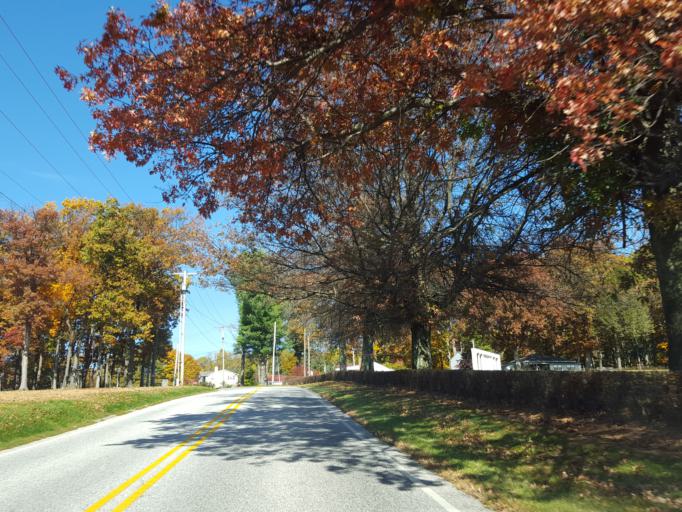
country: US
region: Pennsylvania
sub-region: York County
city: Yoe
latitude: 39.9187
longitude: -76.6582
